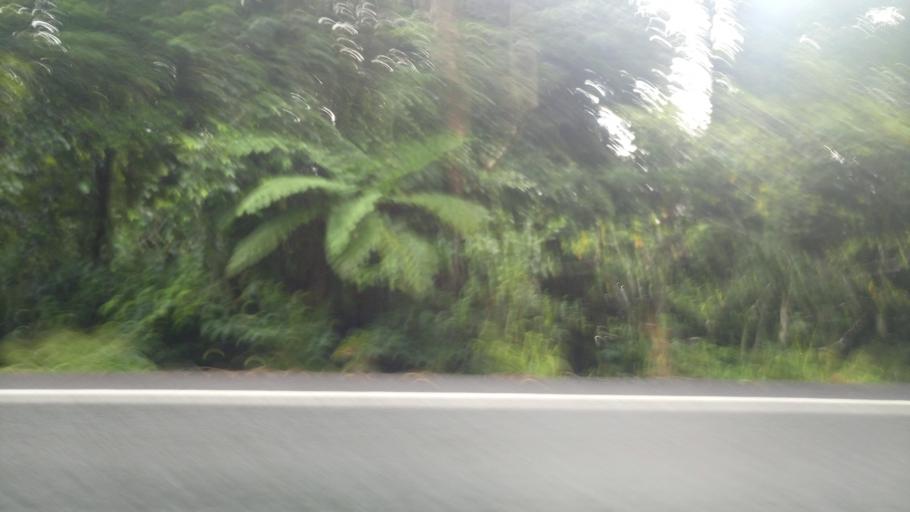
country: AU
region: Queensland
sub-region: Tablelands
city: Ravenshoe
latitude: -17.5747
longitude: 145.6903
